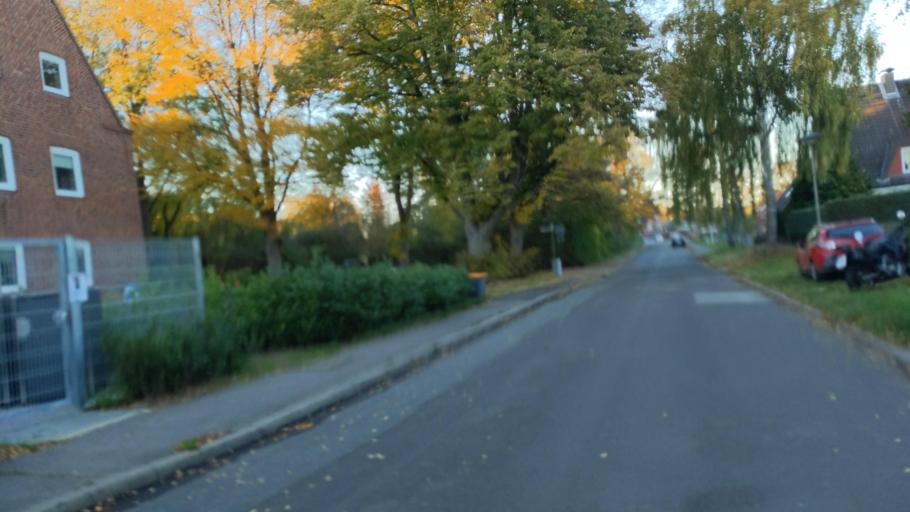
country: DE
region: Schleswig-Holstein
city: Gross Gronau
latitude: 53.8476
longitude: 10.7425
